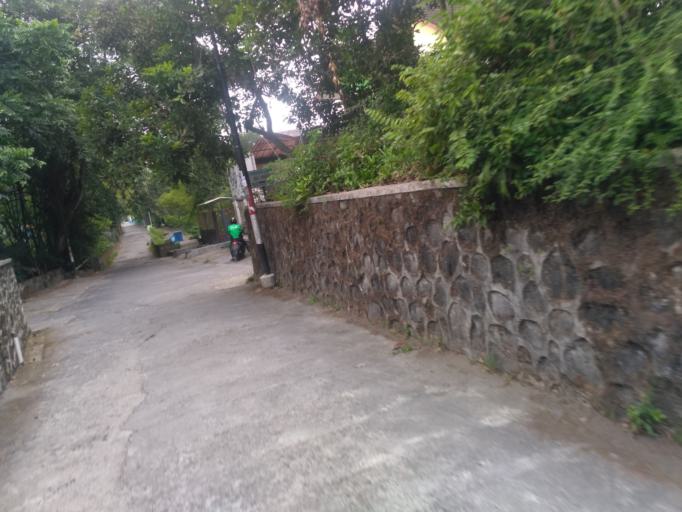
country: ID
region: Daerah Istimewa Yogyakarta
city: Melati
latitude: -7.7518
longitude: 110.3662
